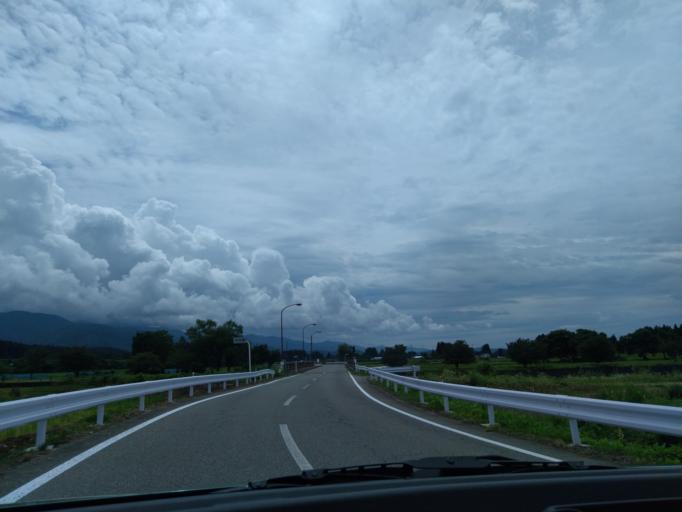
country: JP
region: Akita
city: Kakunodatemachi
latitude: 39.5348
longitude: 140.6410
